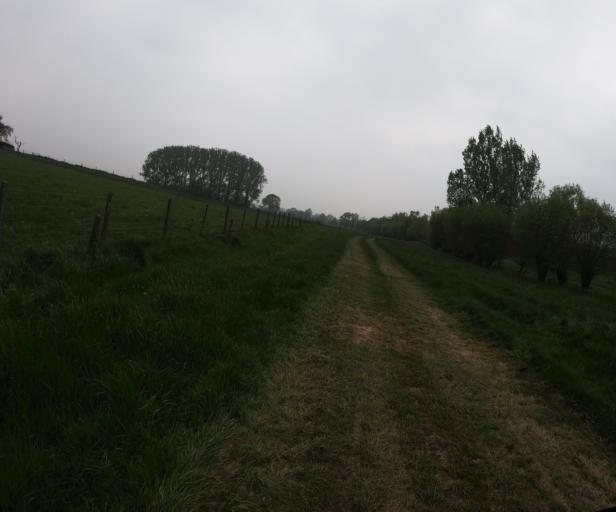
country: BE
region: Flanders
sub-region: Provincie Vlaams-Brabant
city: Pepingen
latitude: 50.7336
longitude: 4.1587
